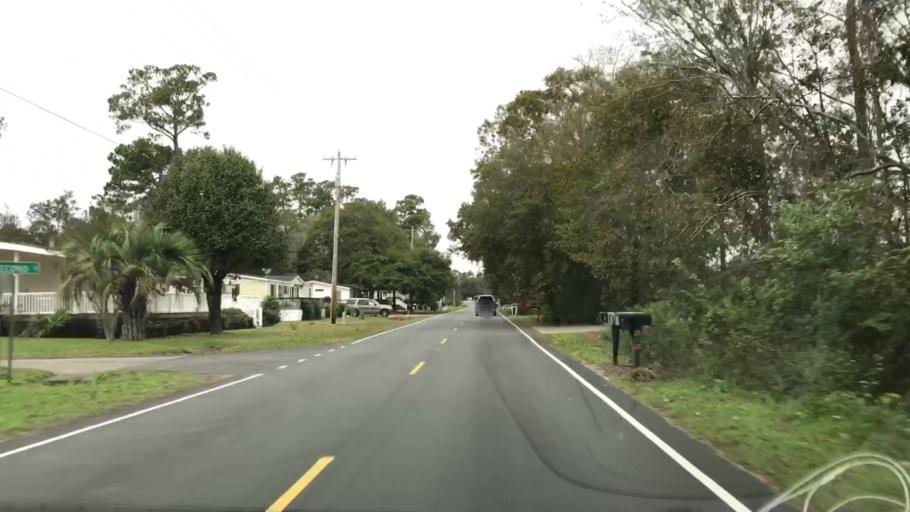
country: US
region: South Carolina
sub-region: Horry County
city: Garden City
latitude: 33.5875
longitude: -79.0029
